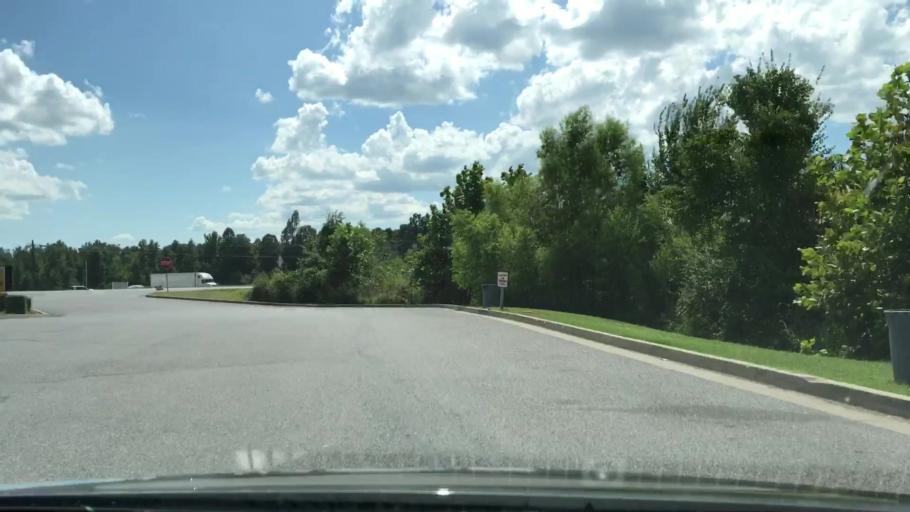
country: US
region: Kentucky
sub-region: Marshall County
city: Calvert City
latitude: 37.0036
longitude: -88.3194
